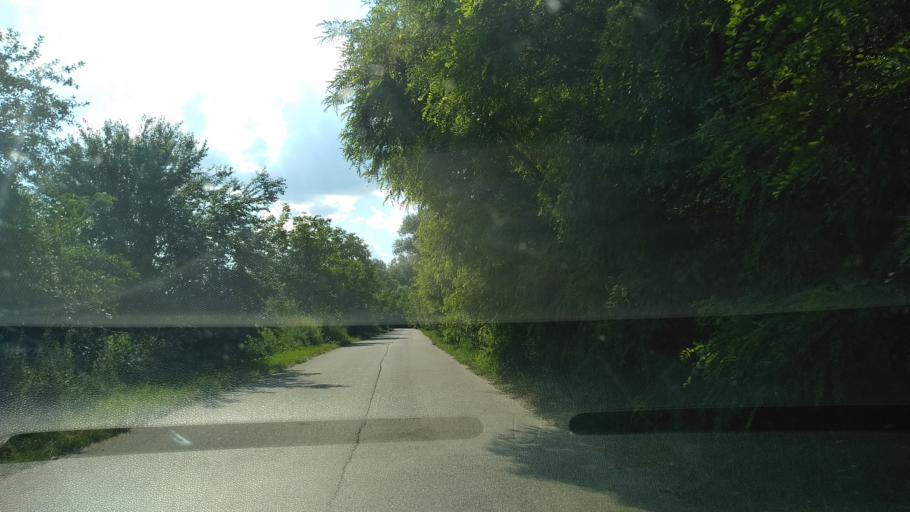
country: RO
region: Hunedoara
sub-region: Comuna Bosorod
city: Bosorod
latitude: 45.7007
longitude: 23.0814
